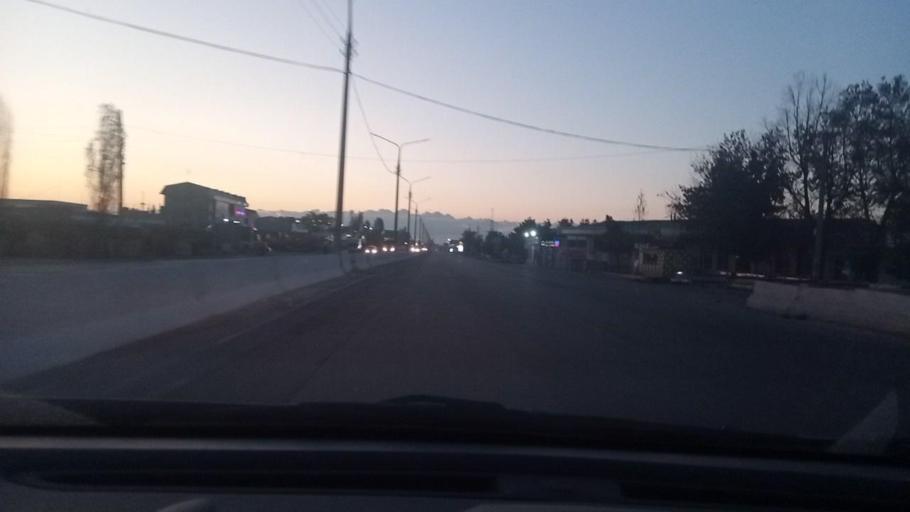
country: UZ
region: Toshkent Shahri
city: Tashkent
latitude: 41.2438
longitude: 69.2245
